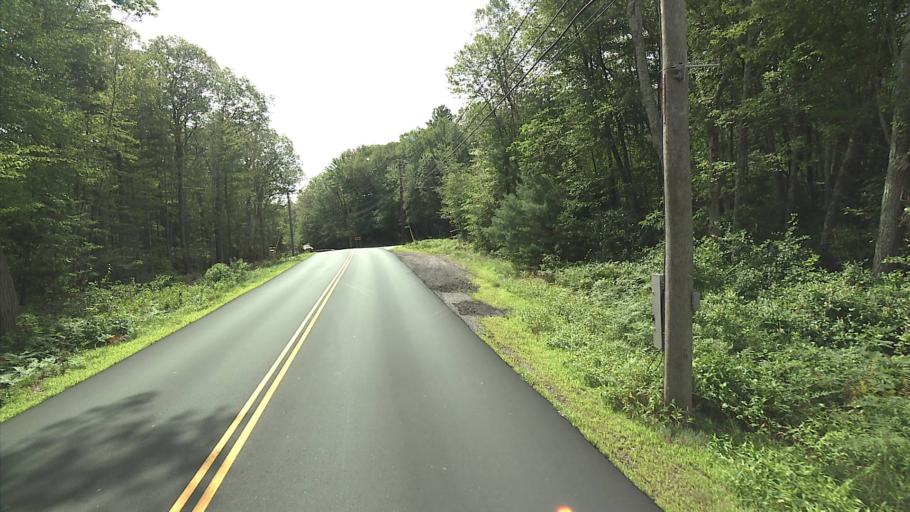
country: US
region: Connecticut
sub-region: Windham County
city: South Woodstock
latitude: 41.9408
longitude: -72.0028
